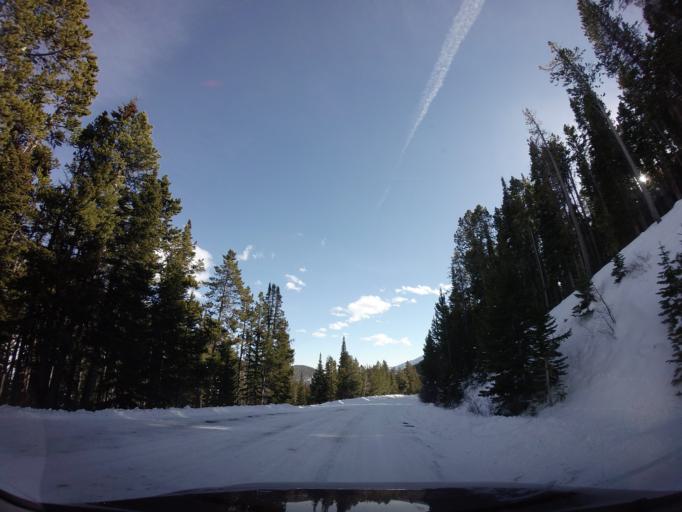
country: US
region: Montana
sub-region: Carbon County
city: Red Lodge
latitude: 45.1895
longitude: -109.3335
